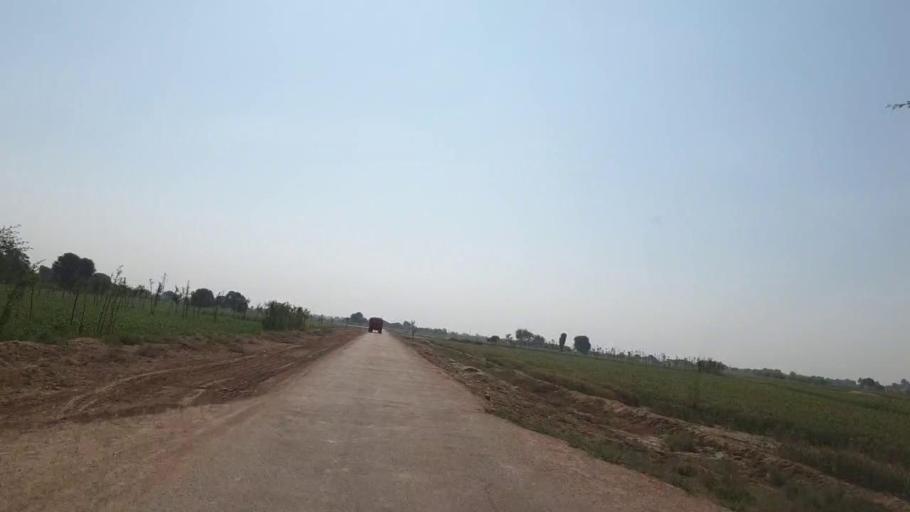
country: PK
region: Sindh
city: Kunri
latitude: 25.1630
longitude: 69.5481
